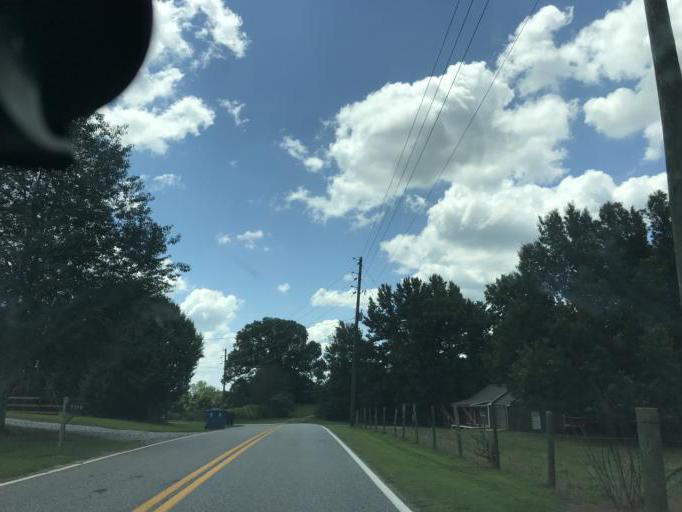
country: US
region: Georgia
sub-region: Fulton County
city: Milton
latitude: 34.2252
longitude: -84.2562
